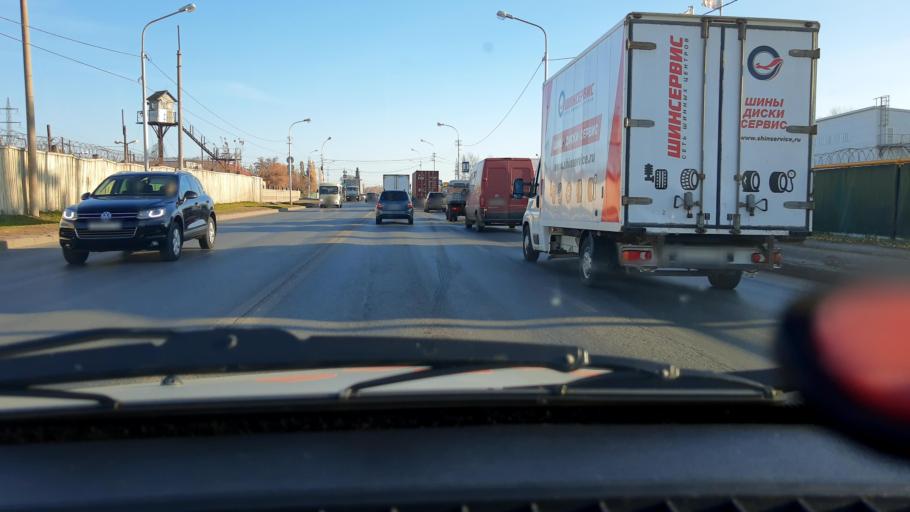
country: RU
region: Bashkortostan
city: Iglino
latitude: 54.7835
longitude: 56.2227
